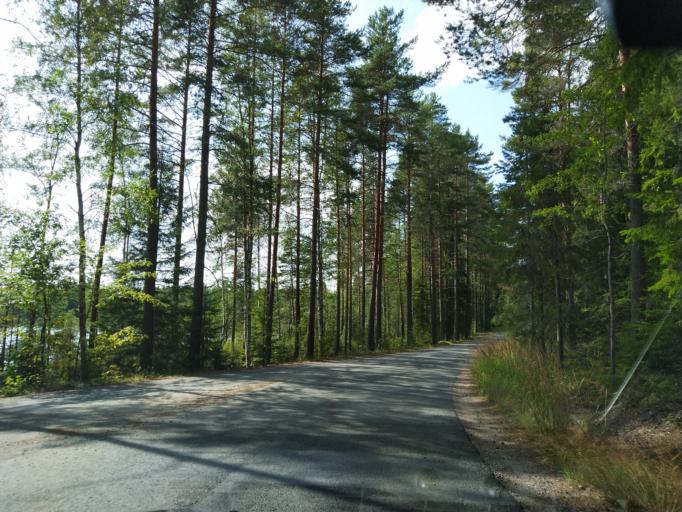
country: FI
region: Uusimaa
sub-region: Helsinki
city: Karkkila
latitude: 60.7175
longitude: 24.1957
